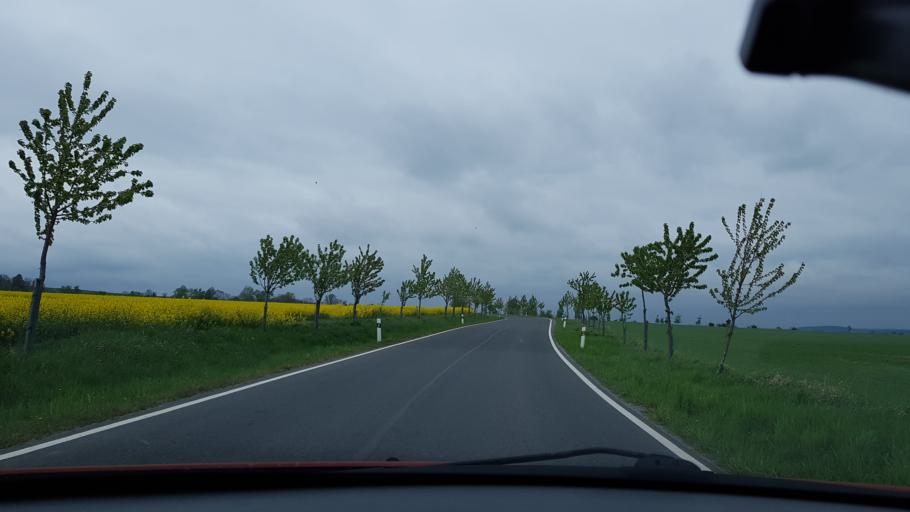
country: CZ
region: Olomoucky
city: Javornik
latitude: 50.4150
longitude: 16.9765
